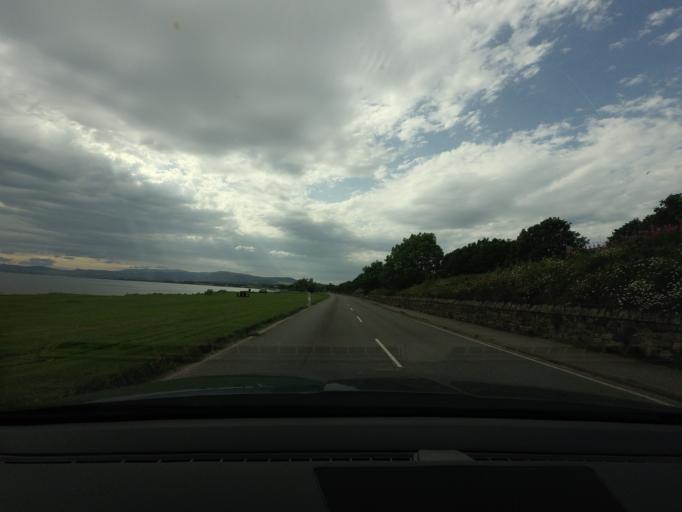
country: GB
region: Scotland
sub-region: Highland
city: Invergordon
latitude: 57.6896
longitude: -4.1816
